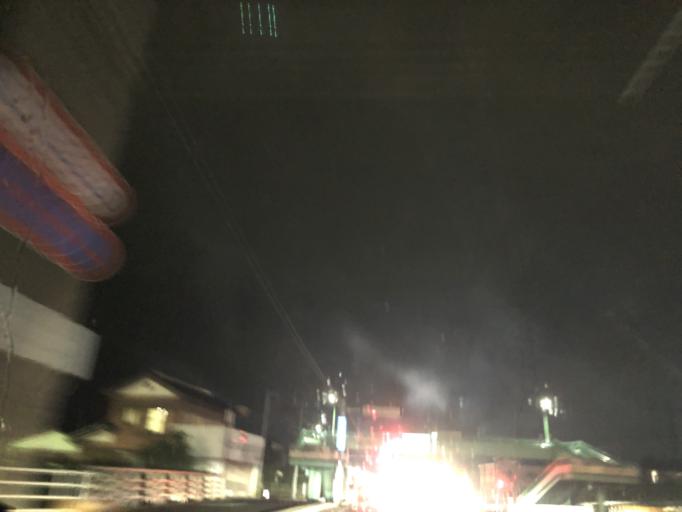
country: JP
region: Tochigi
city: Sano
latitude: 36.3146
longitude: 139.5652
